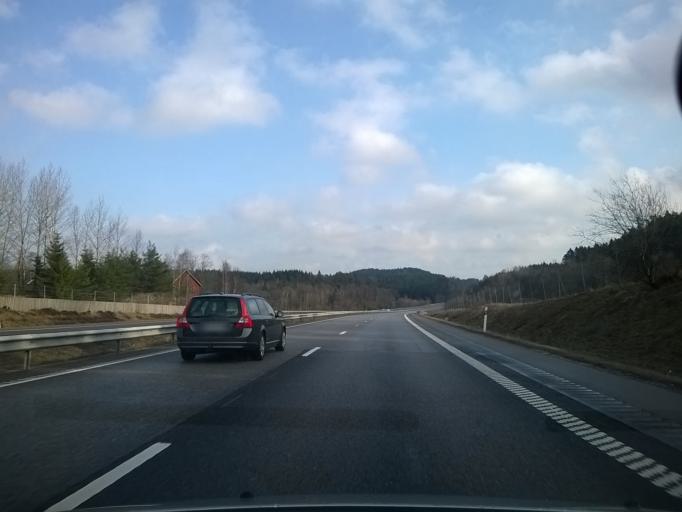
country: SE
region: Vaestra Goetaland
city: Svanesund
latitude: 58.1654
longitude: 11.8904
